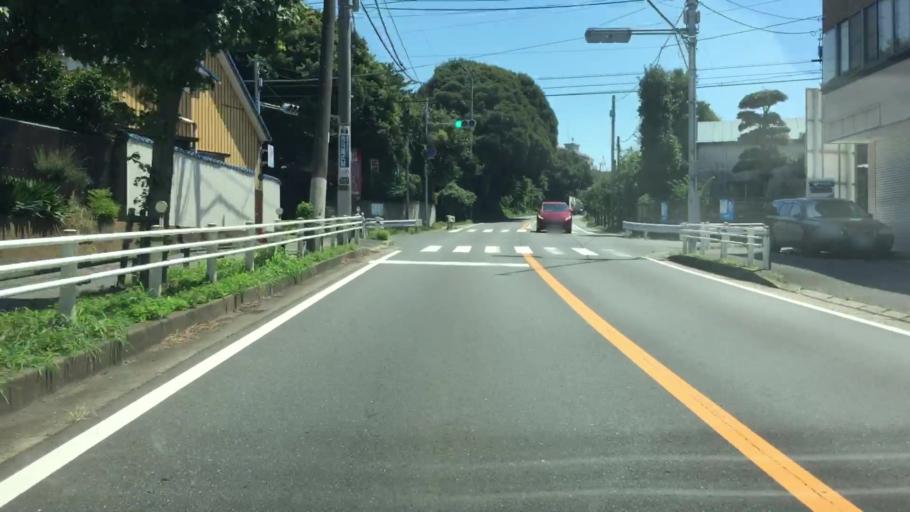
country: JP
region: Chiba
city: Funabashi
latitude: 35.7345
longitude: 139.9583
